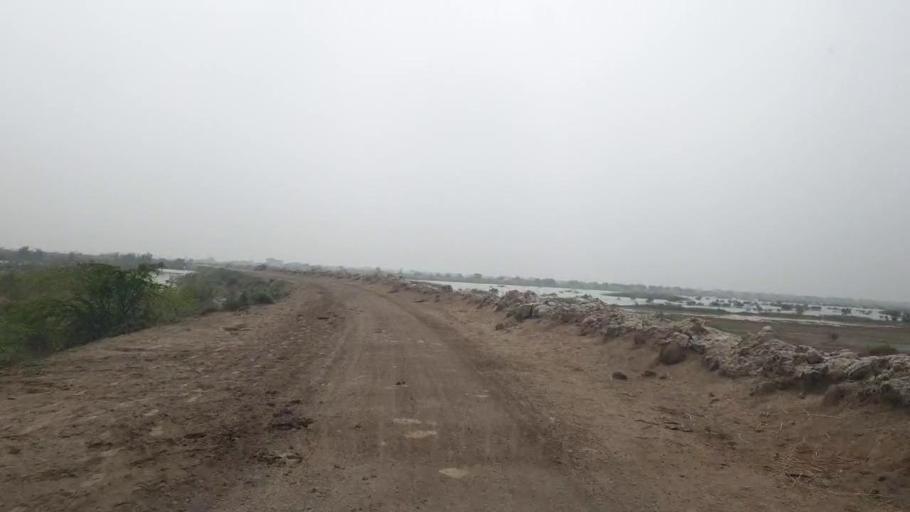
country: PK
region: Sindh
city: Badin
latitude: 24.5798
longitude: 68.6823
